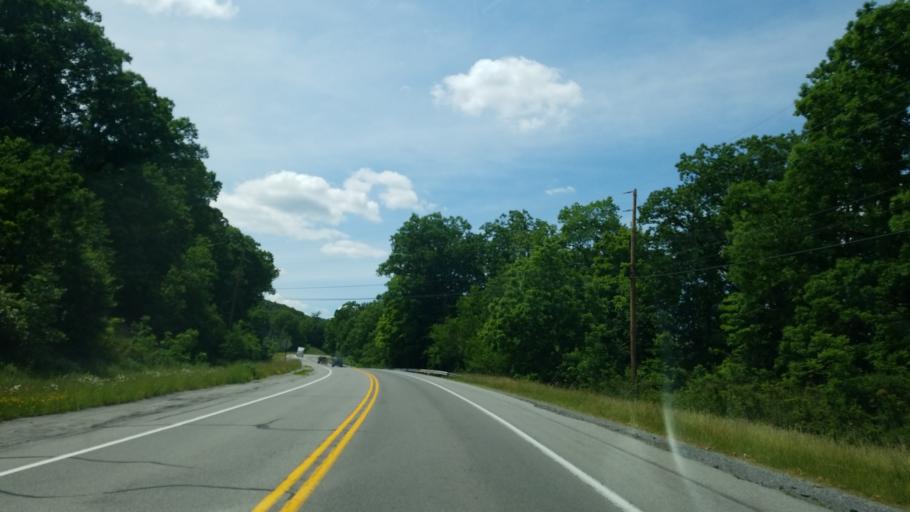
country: US
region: Pennsylvania
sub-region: Blair County
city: Tyrone
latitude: 40.6807
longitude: -78.2579
